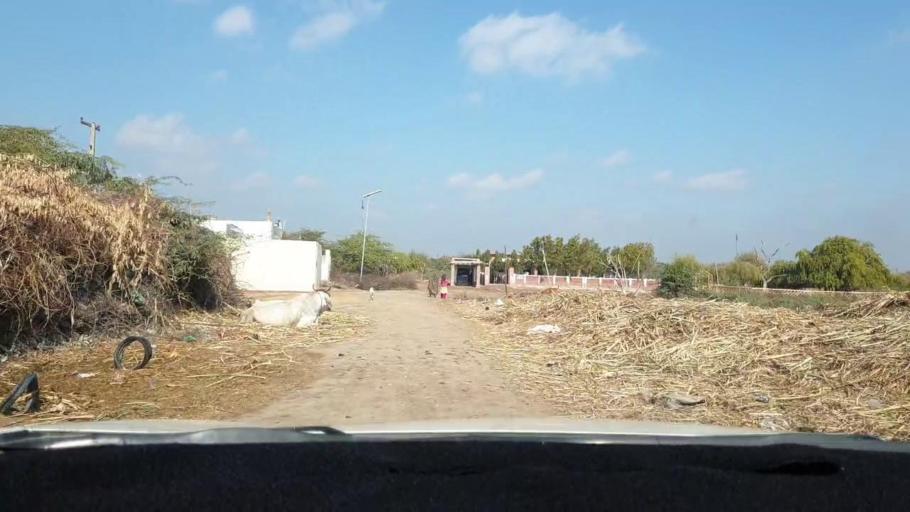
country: PK
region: Sindh
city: Berani
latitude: 25.7294
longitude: 68.9739
